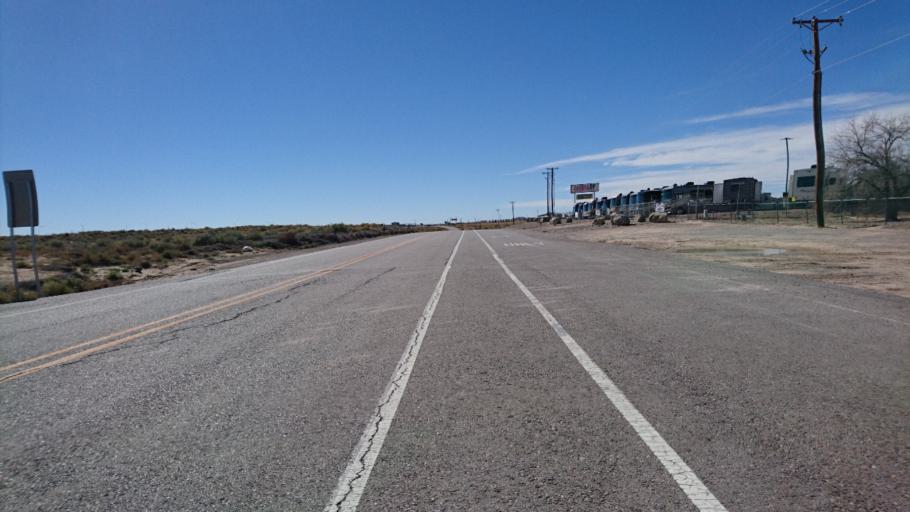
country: US
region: New Mexico
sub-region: Bernalillo County
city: South Valley
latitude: 35.0667
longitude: -106.7903
